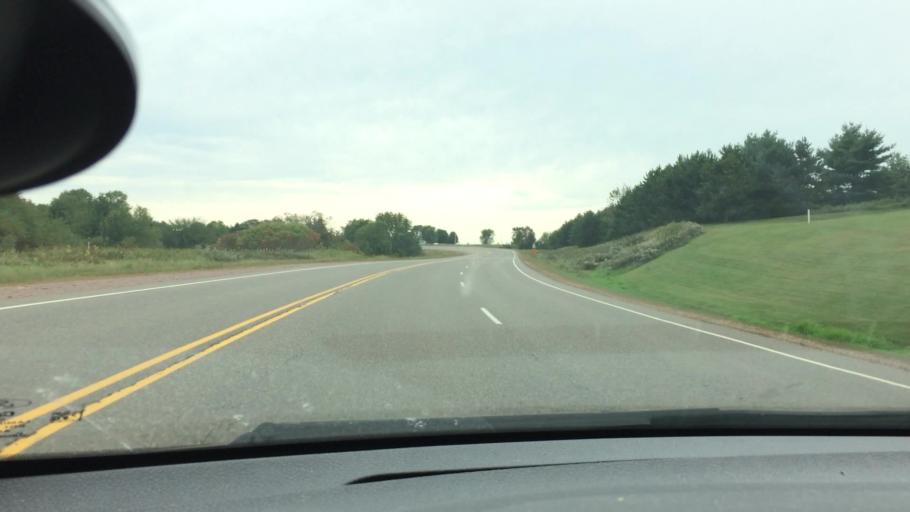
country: US
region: Wisconsin
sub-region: Clark County
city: Neillsville
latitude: 44.5565
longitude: -90.6403
